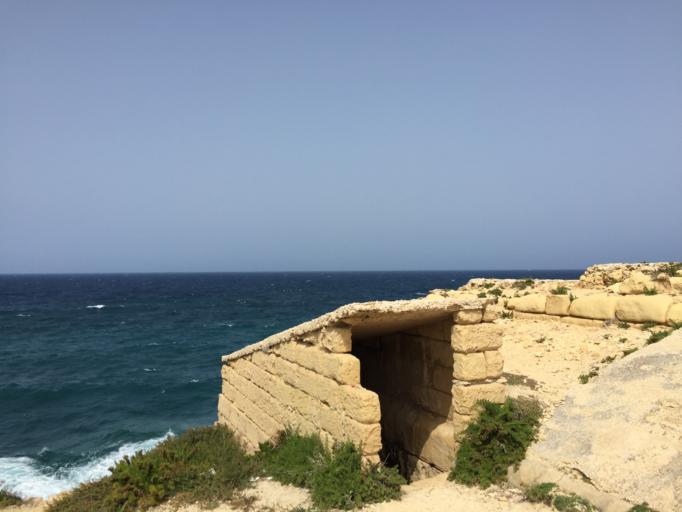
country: MT
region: Il-Kalkara
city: Kalkara
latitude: 35.8971
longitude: 14.5298
